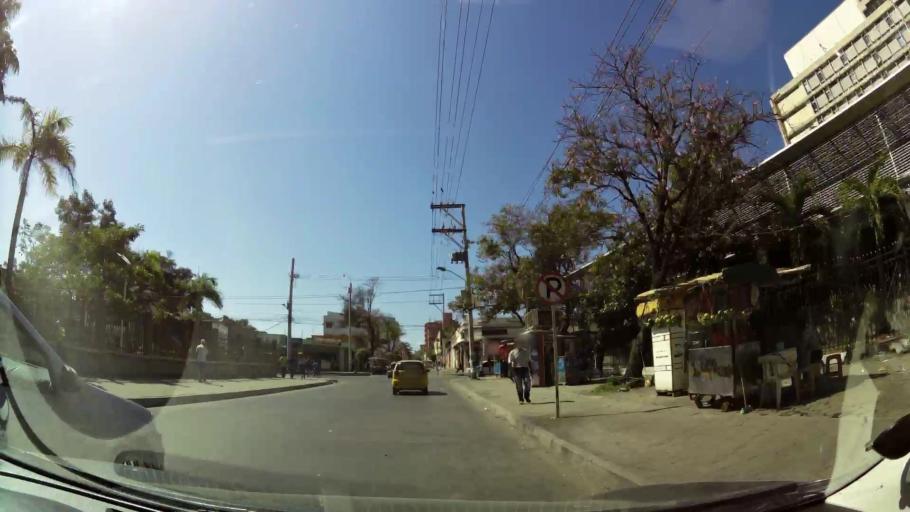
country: CO
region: Atlantico
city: Barranquilla
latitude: 10.9852
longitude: -74.7809
